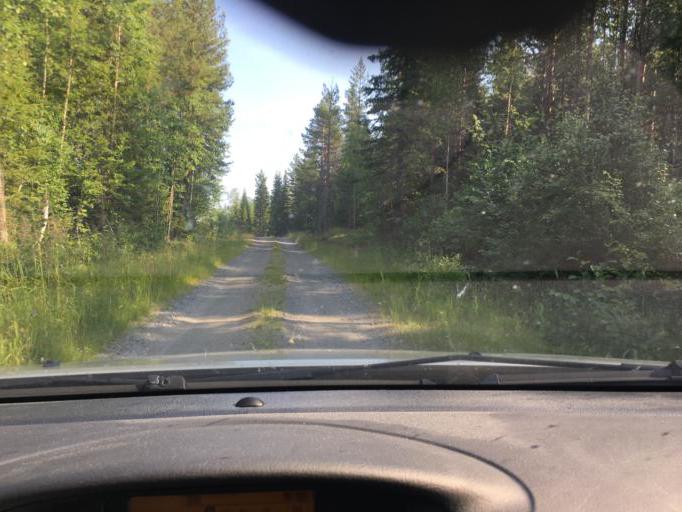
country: SE
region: Norrbotten
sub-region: Kalix Kommun
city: Toere
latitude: 65.8648
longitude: 22.6565
